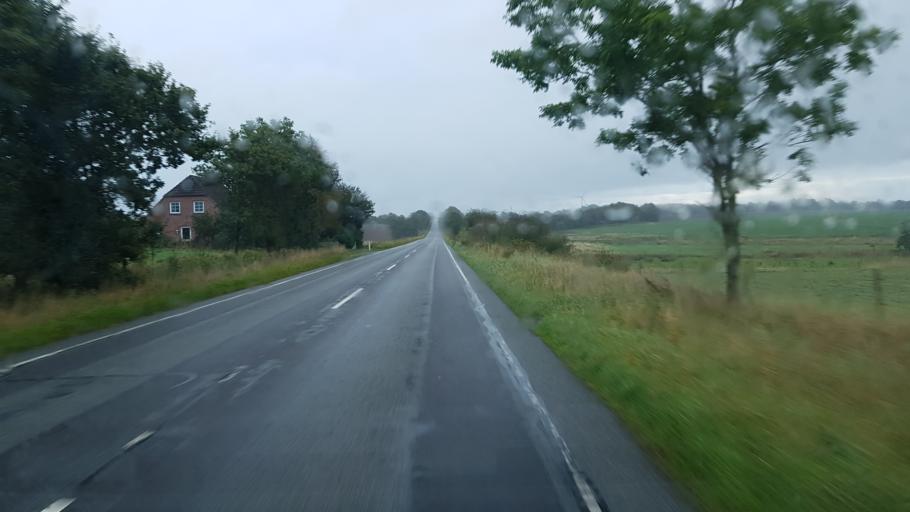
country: DK
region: South Denmark
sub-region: Kolding Kommune
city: Vamdrup
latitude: 55.3468
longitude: 9.2560
